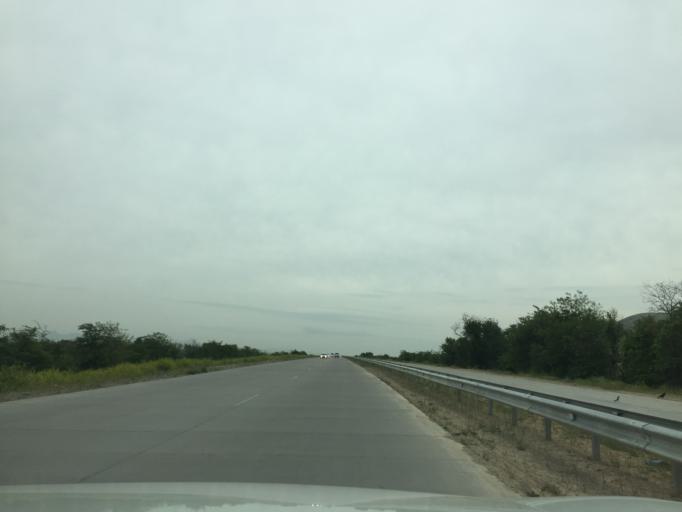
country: KZ
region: Ongtustik Qazaqstan
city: Sastobe
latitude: 42.5418
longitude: 70.0486
